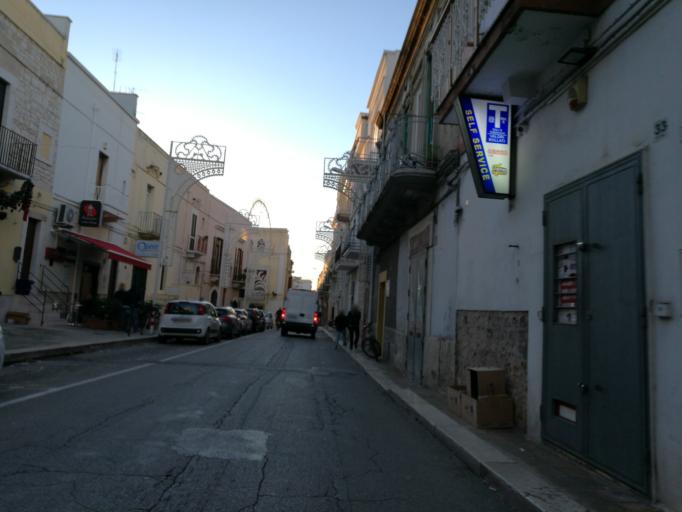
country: IT
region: Apulia
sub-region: Provincia di Bari
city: Adelfia
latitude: 41.0044
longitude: 16.8764
